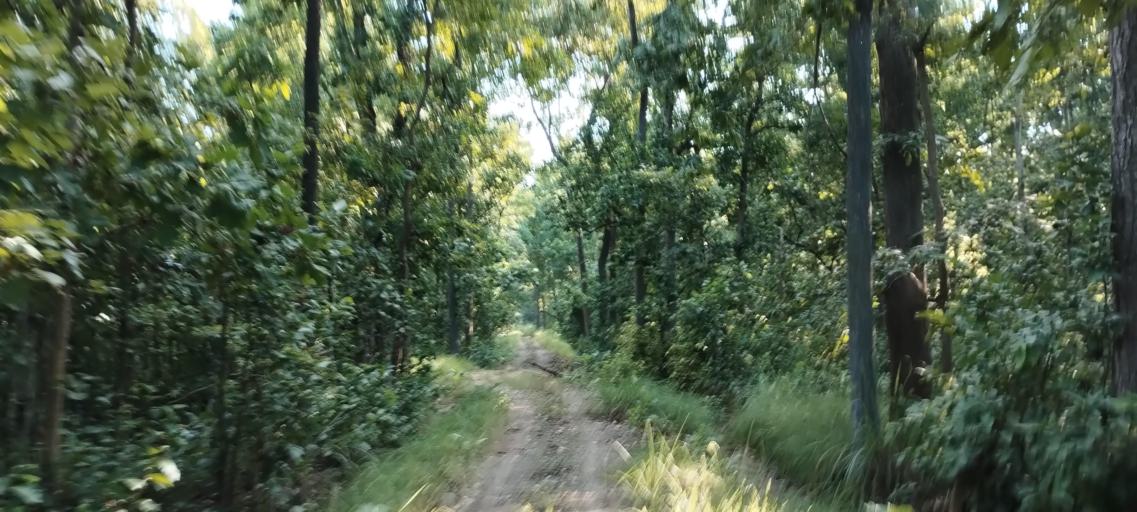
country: NP
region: Far Western
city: Tikapur
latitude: 28.5149
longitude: 81.2726
